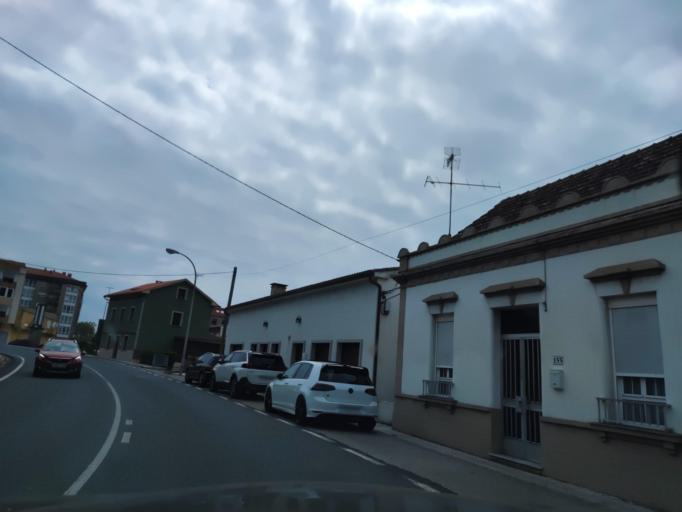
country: ES
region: Galicia
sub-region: Provincia da Coruna
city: Boiro
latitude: 42.6456
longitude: -8.8923
